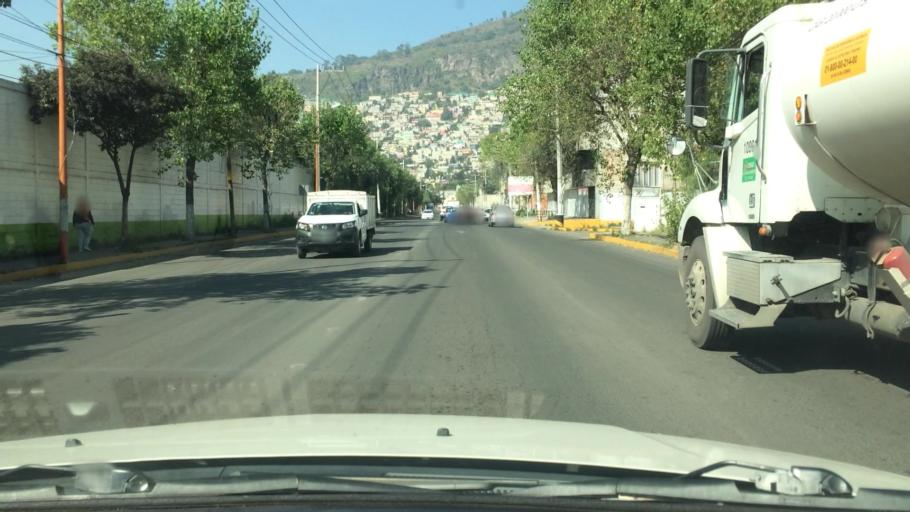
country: MX
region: Mexico
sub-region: Tlalnepantla de Baz
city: Puerto Escondido (Tepeolulco Puerto Escondido)
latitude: 19.5269
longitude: -99.1156
